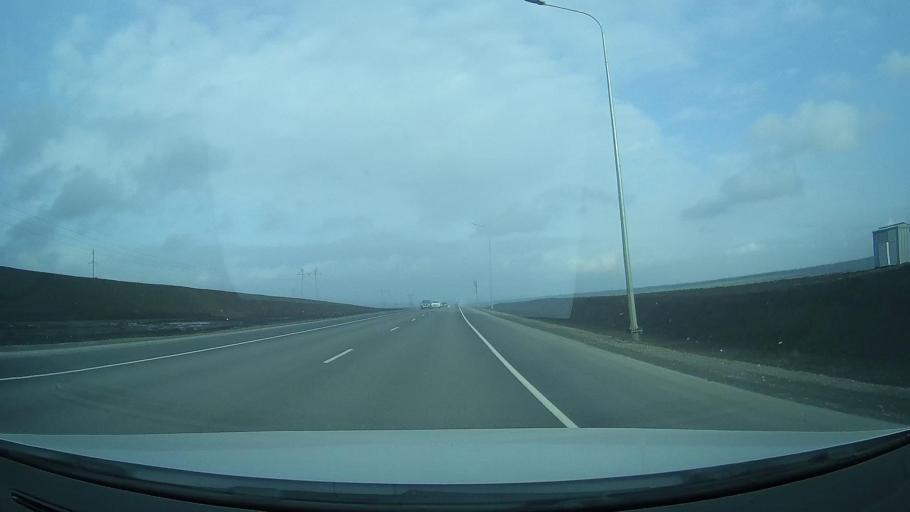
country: RU
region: Rostov
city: Grushevskaya
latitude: 47.3898
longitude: 39.8472
